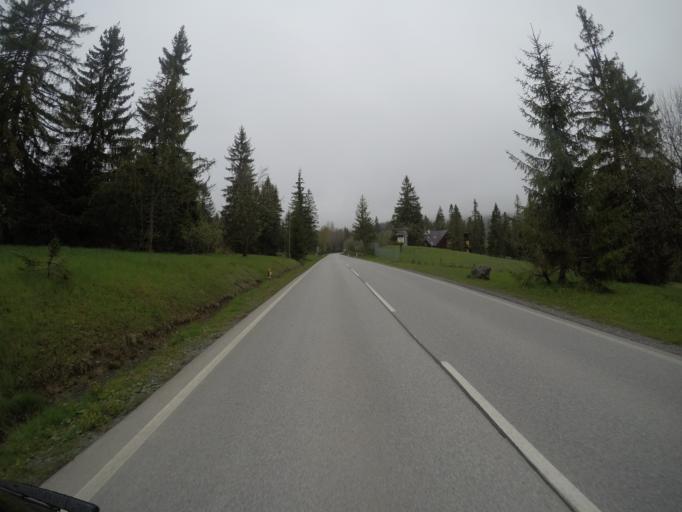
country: SK
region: Presovsky
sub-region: Okres Poprad
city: Strba
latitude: 49.0921
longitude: 20.0701
